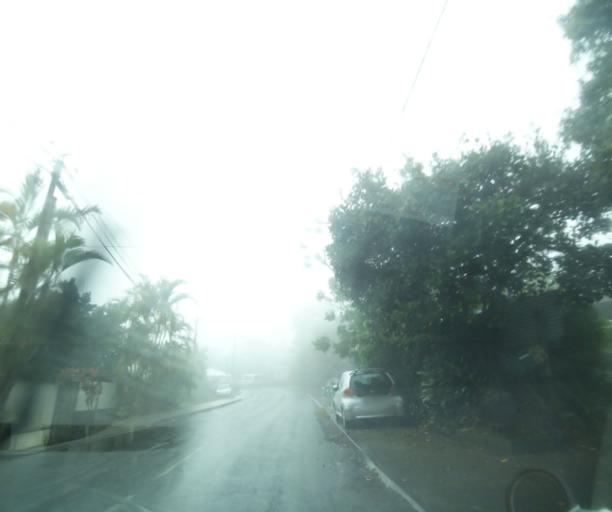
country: RE
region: Reunion
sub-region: Reunion
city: Saint-Paul
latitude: -21.0085
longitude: 55.3191
